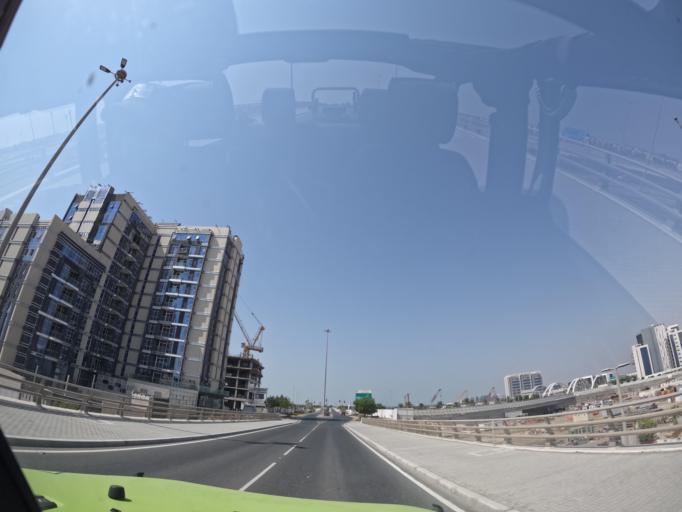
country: AE
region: Abu Dhabi
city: Abu Dhabi
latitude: 24.4435
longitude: 54.5921
